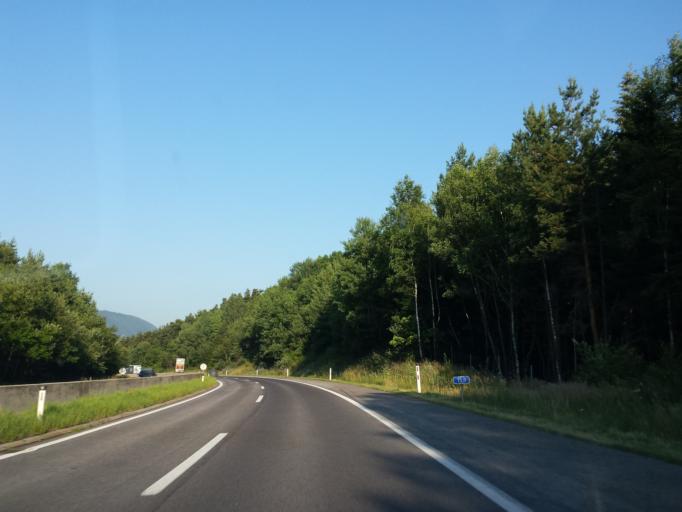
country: AT
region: Lower Austria
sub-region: Politischer Bezirk Neunkirchen
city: Enzenreith
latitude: 47.6663
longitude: 15.9648
